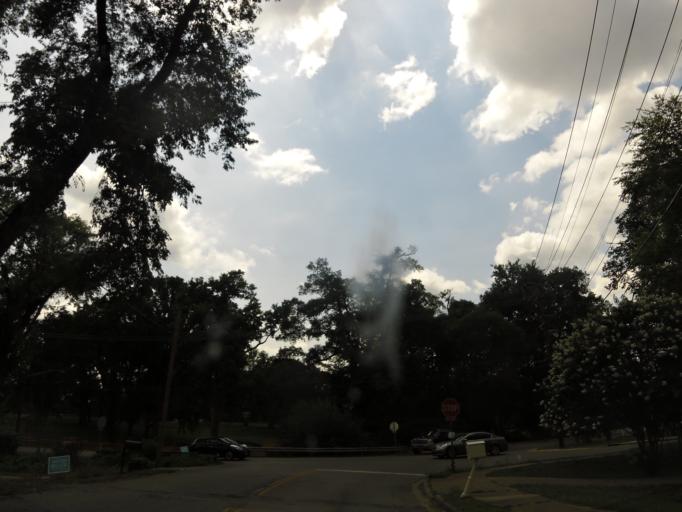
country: US
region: Tennessee
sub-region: Davidson County
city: Oak Hill
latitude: 36.1196
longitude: -86.7869
